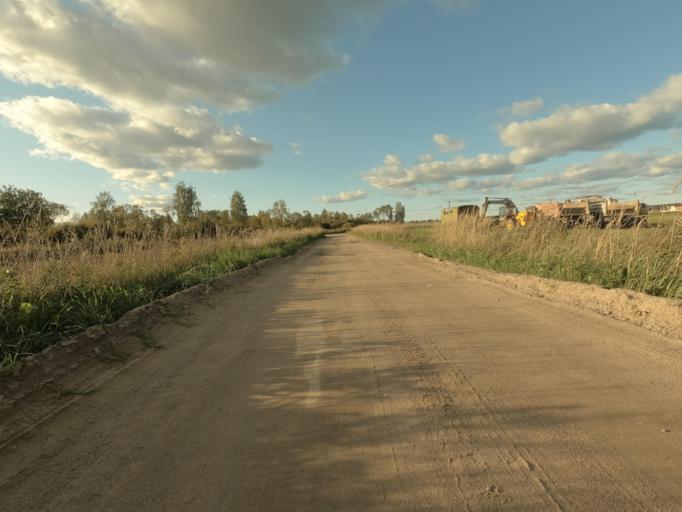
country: RU
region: Leningrad
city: Imeni Sverdlova
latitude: 59.8648
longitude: 30.7298
